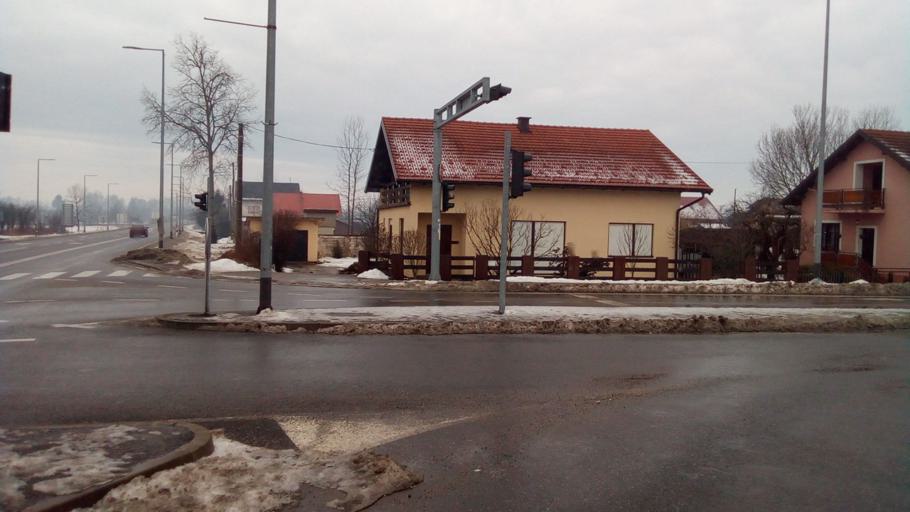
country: HR
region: Zagrebacka
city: Lupoglav
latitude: 45.6984
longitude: 16.3990
